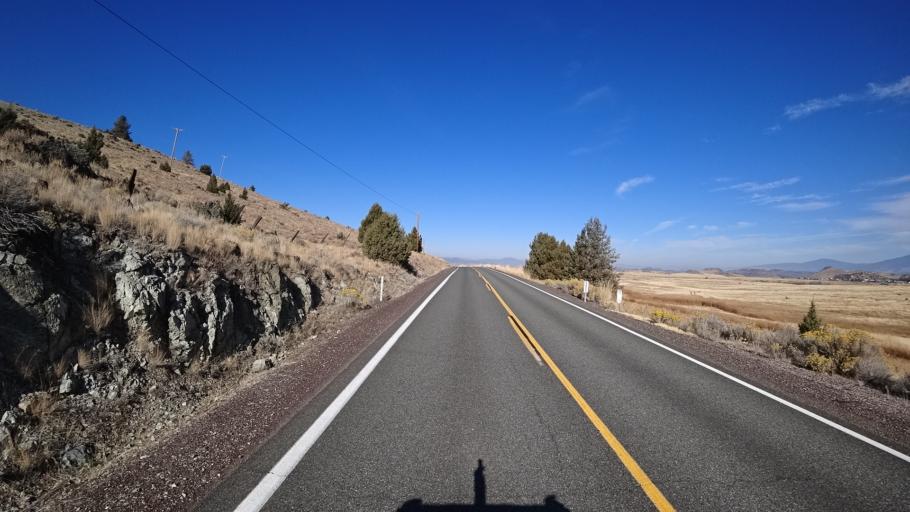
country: US
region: California
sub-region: Siskiyou County
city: Weed
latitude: 41.4655
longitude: -122.4659
